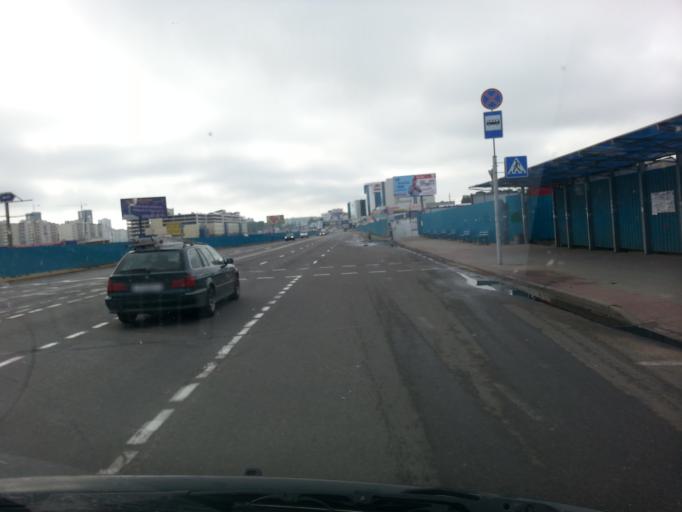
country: BY
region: Minsk
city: Zhdanovichy
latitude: 53.9361
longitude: 27.4510
